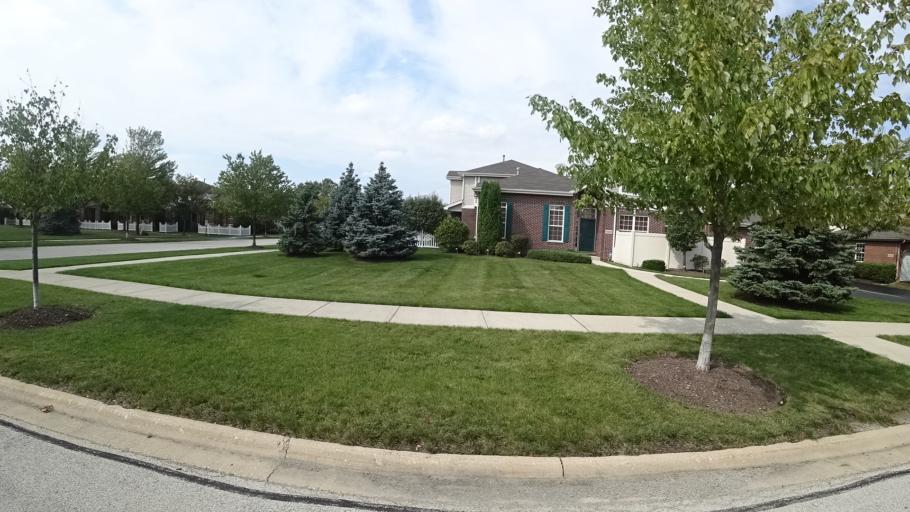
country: US
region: Illinois
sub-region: Cook County
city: Tinley Park
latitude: 41.5526
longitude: -87.7801
